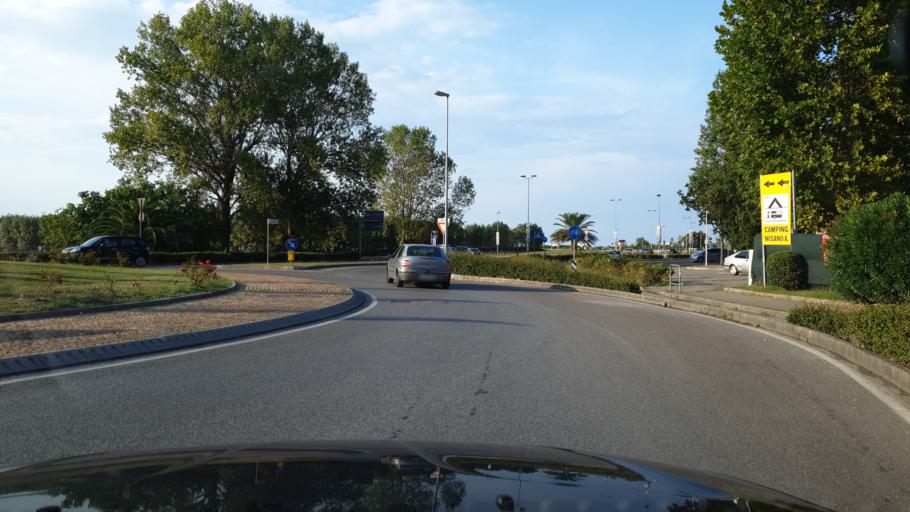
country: IT
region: Emilia-Romagna
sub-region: Provincia di Rimini
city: Montalbano
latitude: 43.9705
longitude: 12.7123
